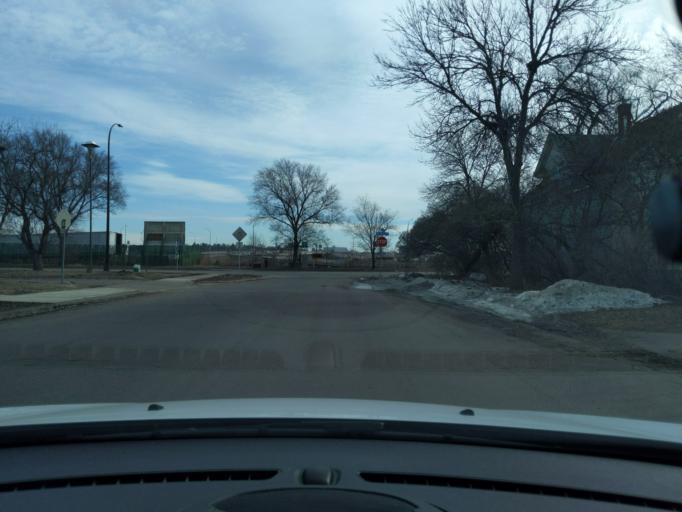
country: US
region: Minnesota
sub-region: Hennepin County
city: Saint Anthony
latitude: 45.0017
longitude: -93.2378
